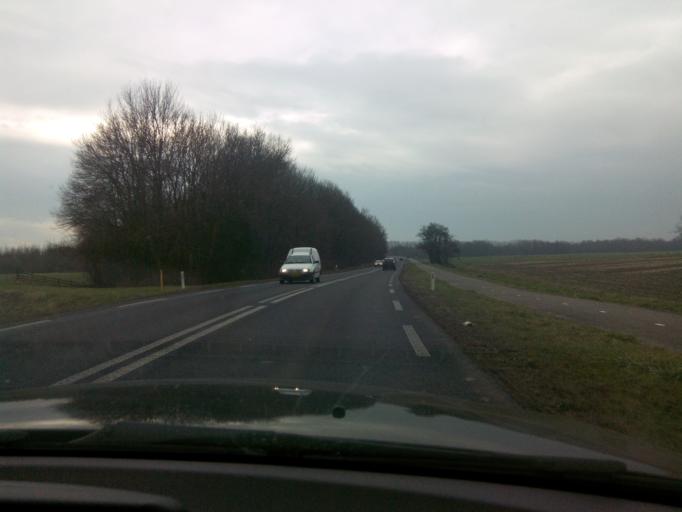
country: NL
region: South Holland
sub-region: Gemeente Leerdam
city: Leerdam
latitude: 51.8750
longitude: 5.0938
